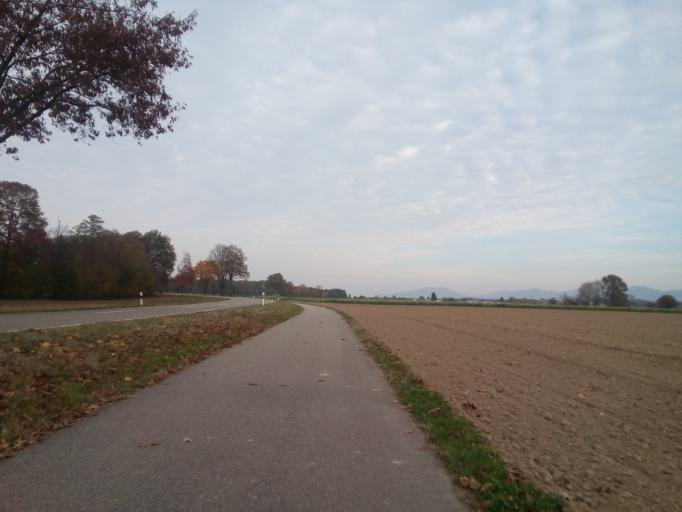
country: DE
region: Baden-Wuerttemberg
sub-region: Karlsruhe Region
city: Zell
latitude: 48.6799
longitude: 8.0383
